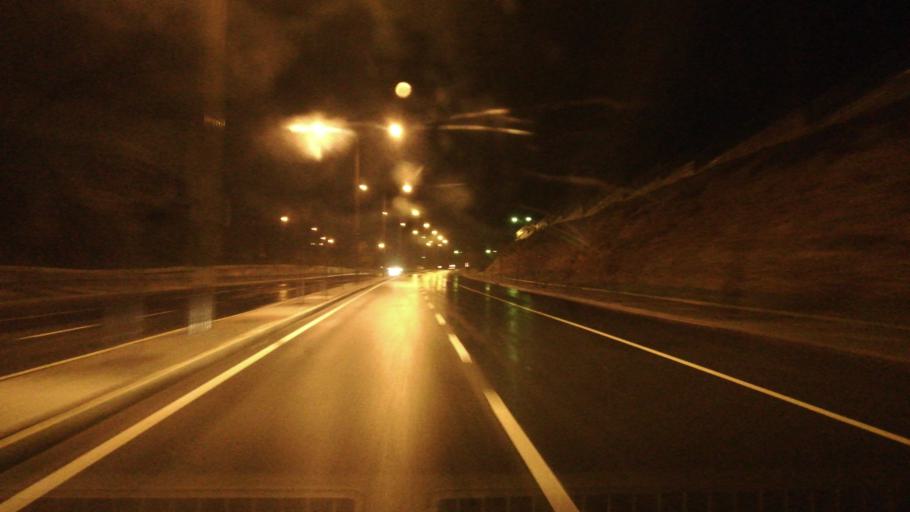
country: TR
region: Kahramanmaras
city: Kahramanmaras
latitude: 37.5964
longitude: 36.9251
